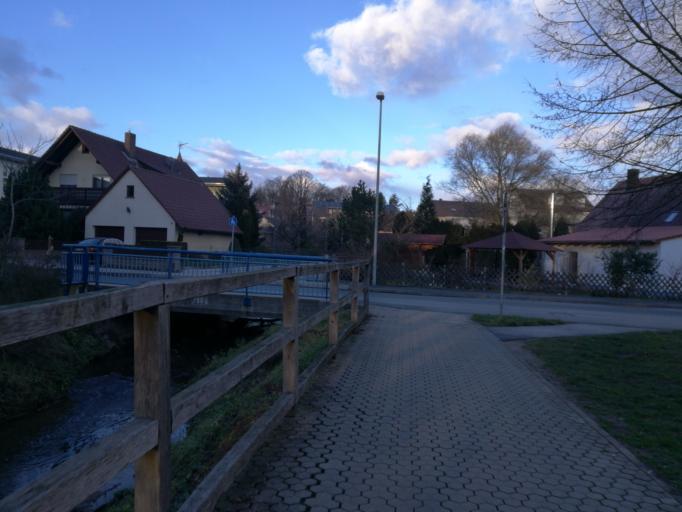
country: DE
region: Bavaria
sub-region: Regierungsbezirk Mittelfranken
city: Veitsbronn
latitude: 49.5099
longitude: 10.8855
